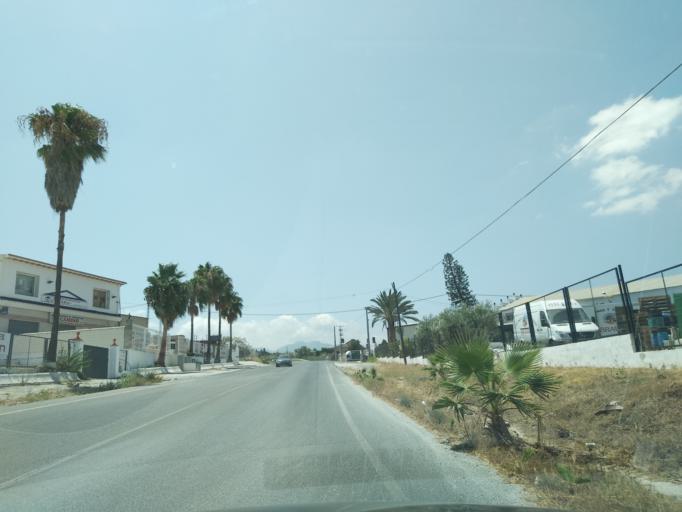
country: ES
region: Andalusia
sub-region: Provincia de Malaga
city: Alhaurin el Grande
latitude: 36.6560
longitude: -4.6760
